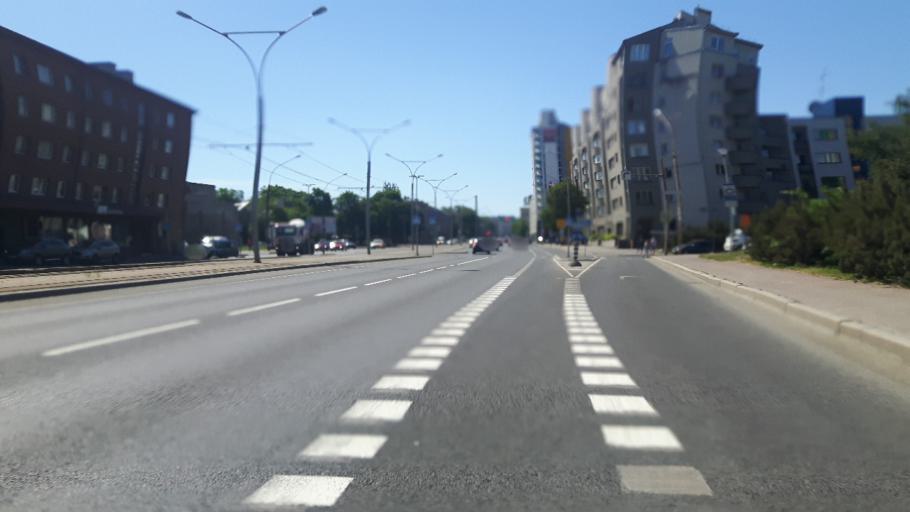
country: EE
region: Harju
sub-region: Tallinna linn
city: Tallinn
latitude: 59.4168
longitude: 24.7402
